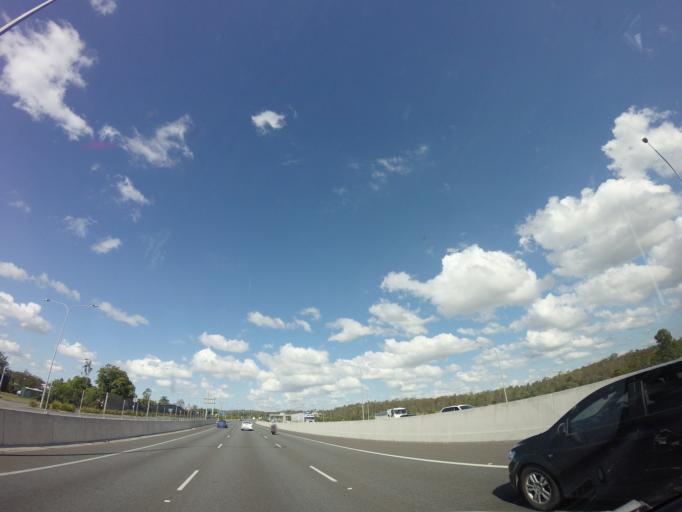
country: AU
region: Queensland
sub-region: Ipswich
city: Redbank
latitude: -27.6027
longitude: 152.8711
